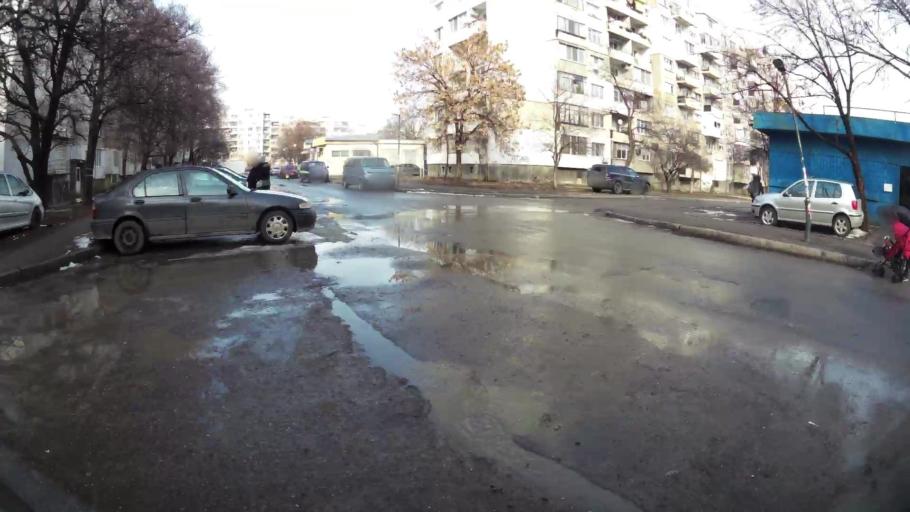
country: BG
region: Sofia-Capital
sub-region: Stolichna Obshtina
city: Sofia
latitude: 42.7184
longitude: 23.2644
